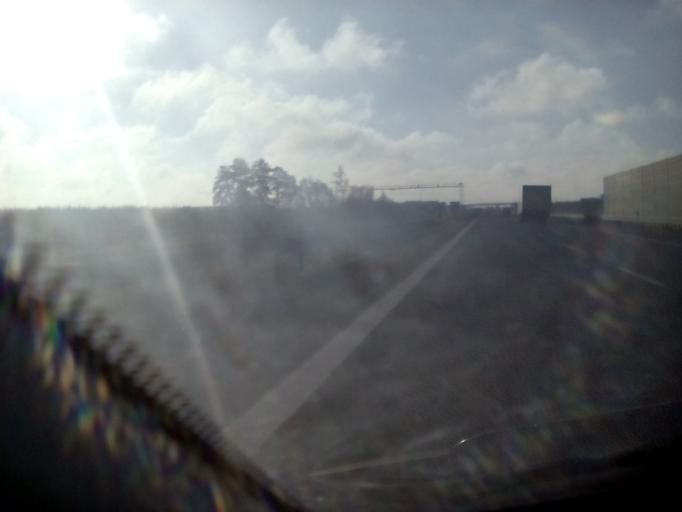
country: PL
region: Masovian Voivodeship
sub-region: Powiat grojecki
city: Jasieniec
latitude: 51.7969
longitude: 20.8903
